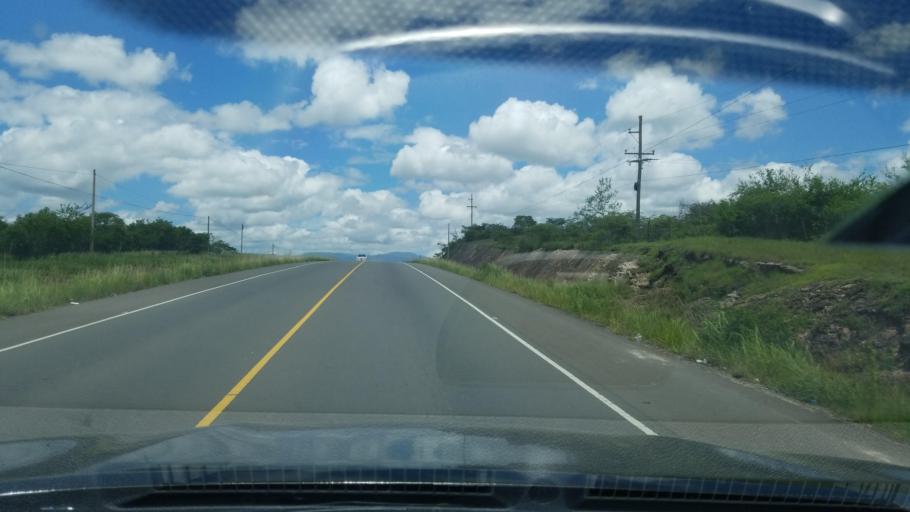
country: HN
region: Francisco Morazan
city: Cofradia
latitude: 14.2984
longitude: -87.2369
